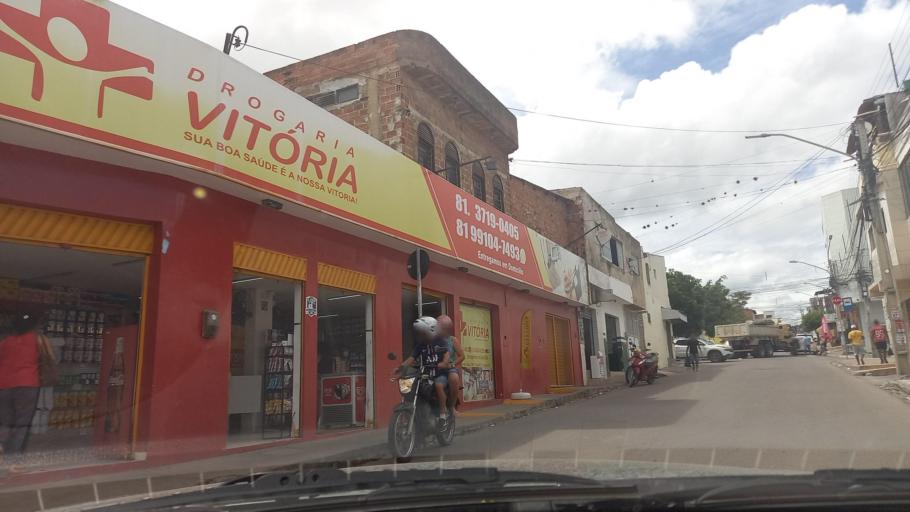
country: BR
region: Pernambuco
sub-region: Caruaru
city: Caruaru
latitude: -8.2718
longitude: -35.9596
